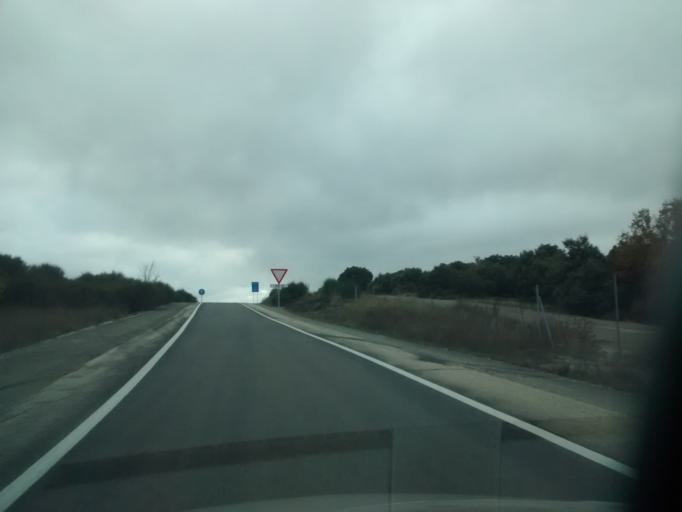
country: ES
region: Castille-La Mancha
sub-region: Provincia de Guadalajara
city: Sauca
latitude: 41.0100
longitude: -2.5608
